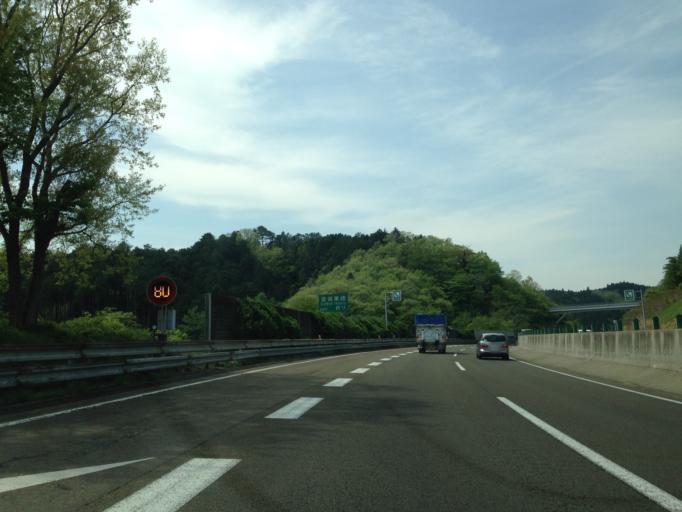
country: JP
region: Miyagi
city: Sendai
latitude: 38.2304
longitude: 140.8098
